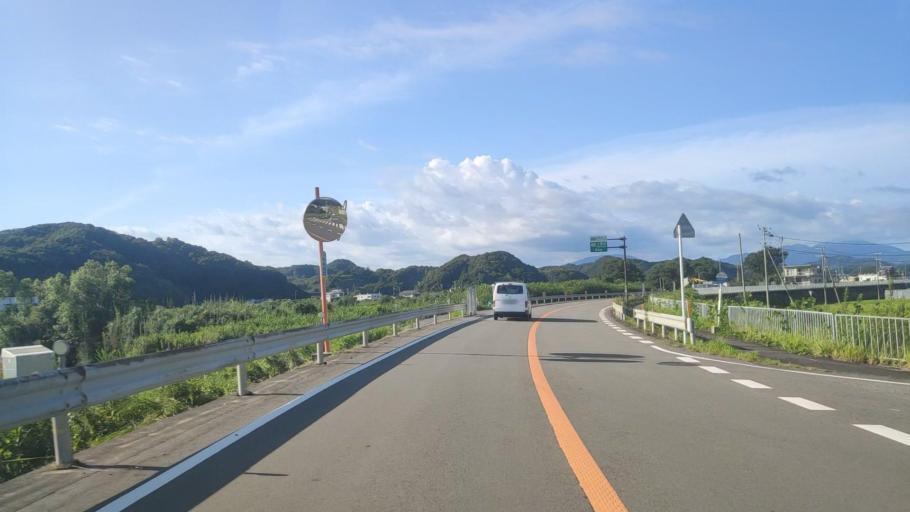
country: JP
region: Wakayama
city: Tanabe
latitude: 33.6765
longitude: 135.4076
